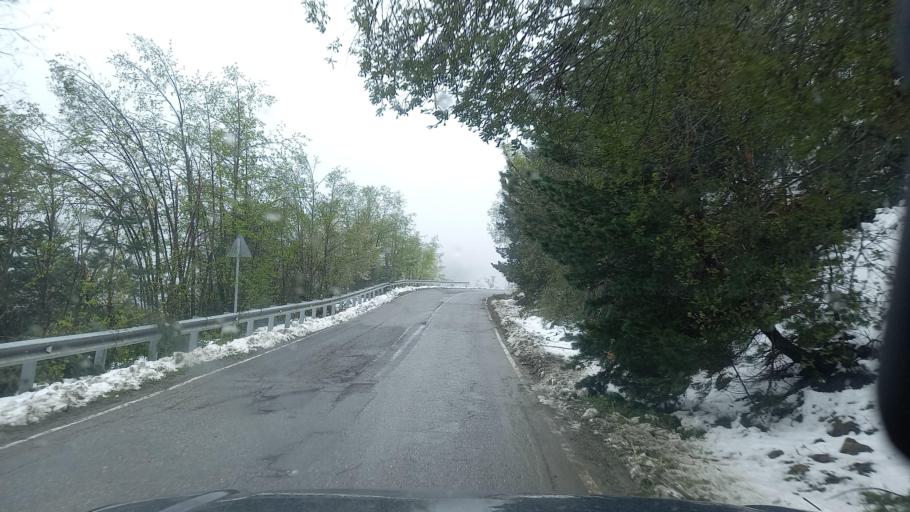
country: RU
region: North Ossetia
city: Mizur
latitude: 42.8000
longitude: 43.9342
